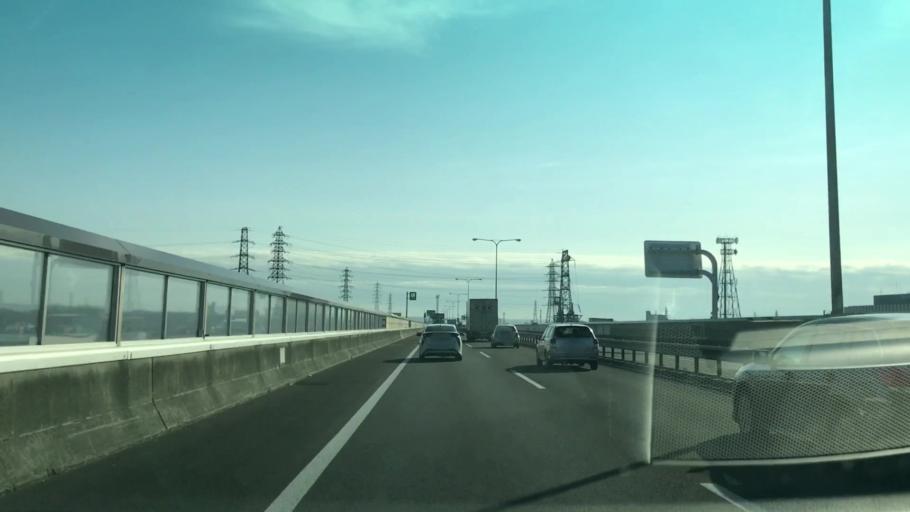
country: JP
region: Hokkaido
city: Sapporo
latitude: 43.0947
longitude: 141.4003
